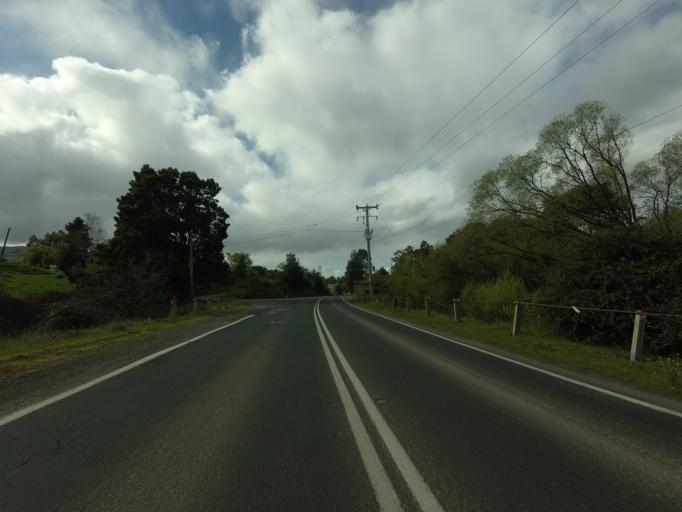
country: AU
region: Tasmania
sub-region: Huon Valley
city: Franklin
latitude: -43.0745
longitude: 147.0167
